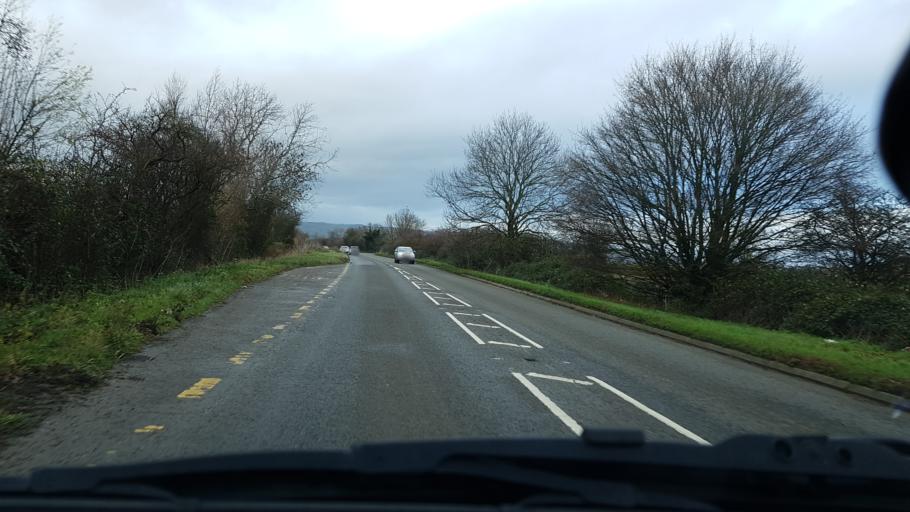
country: GB
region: England
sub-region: Gloucestershire
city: Gotherington
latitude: 51.9796
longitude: -2.0718
